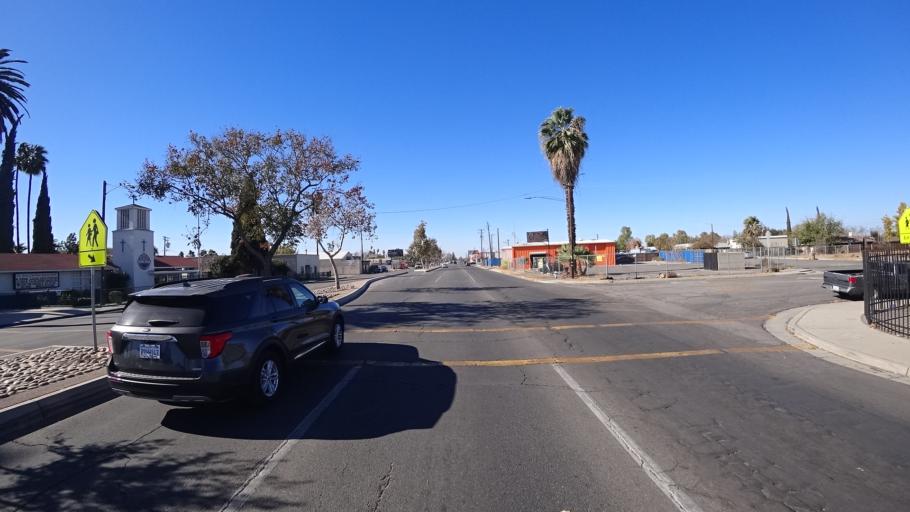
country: US
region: California
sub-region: Kern County
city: Bakersfield
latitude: 35.3685
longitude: -118.9974
